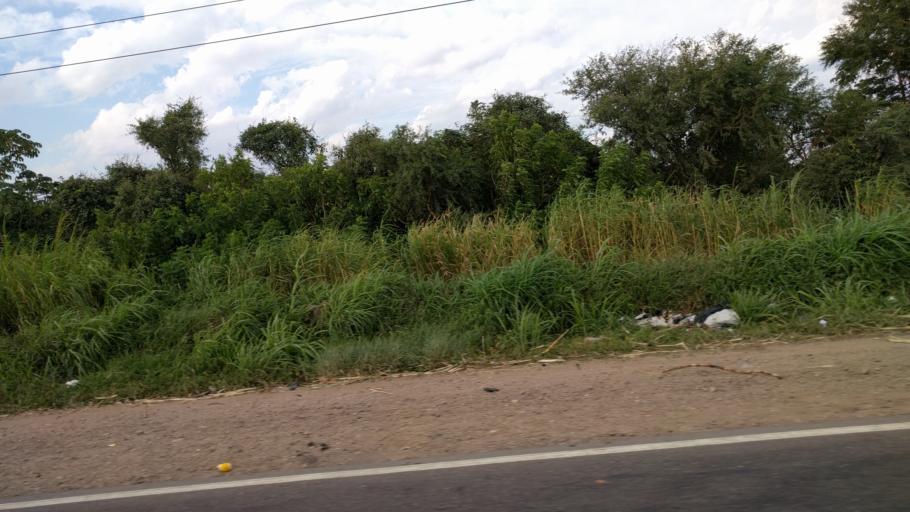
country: BO
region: Santa Cruz
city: Warnes
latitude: -17.5445
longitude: -63.1604
